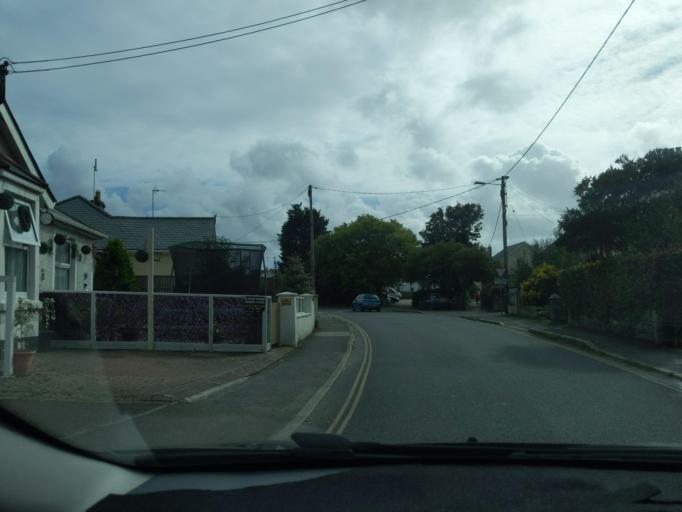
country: GB
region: England
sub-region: Cornwall
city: Par
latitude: 50.3527
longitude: -4.7003
